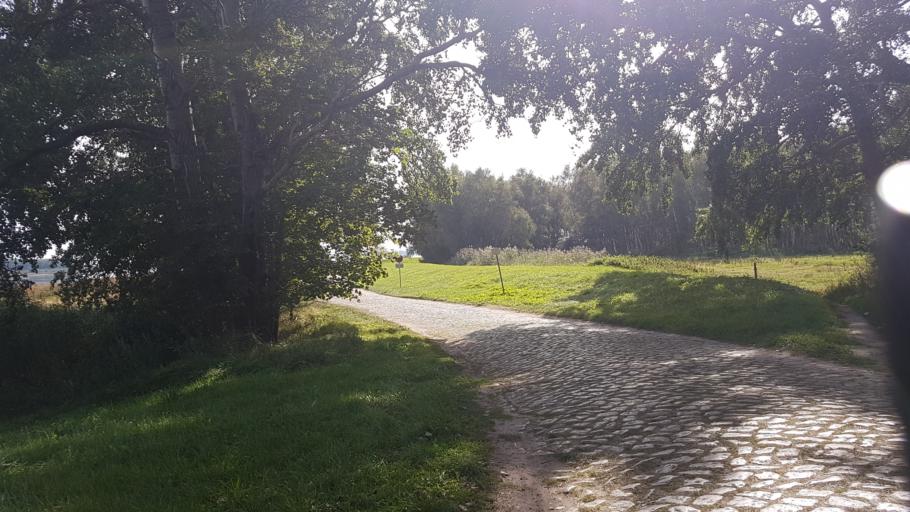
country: DE
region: Mecklenburg-Vorpommern
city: Gingst
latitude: 54.4313
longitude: 13.2060
